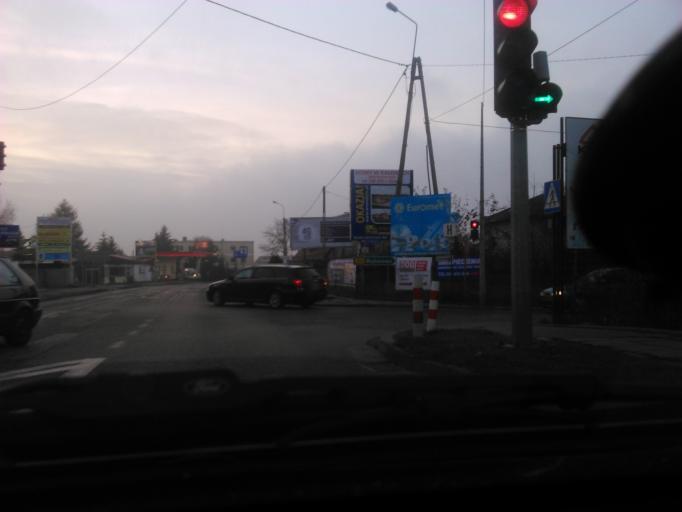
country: PL
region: Pomeranian Voivodeship
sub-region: Powiat kartuski
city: Kartuzy
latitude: 54.3305
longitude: 18.2076
